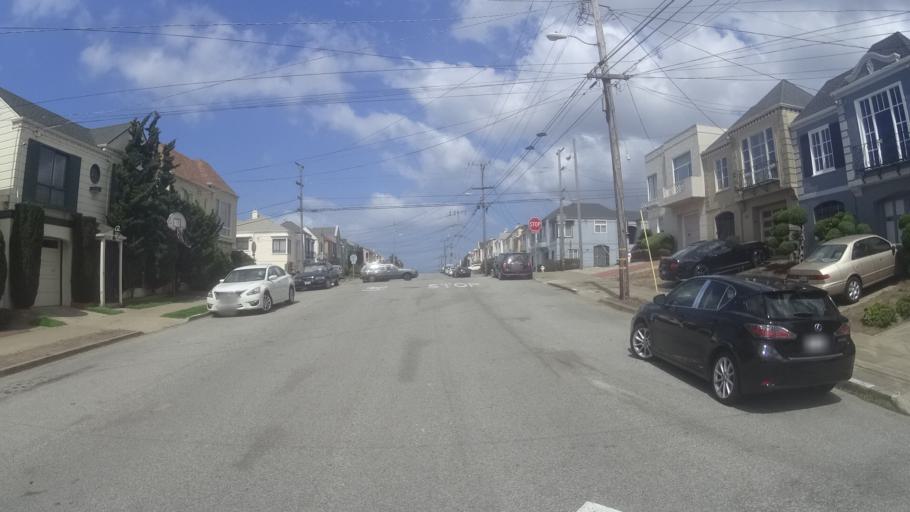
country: US
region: California
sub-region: San Mateo County
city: Daly City
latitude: 37.7550
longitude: -122.4926
